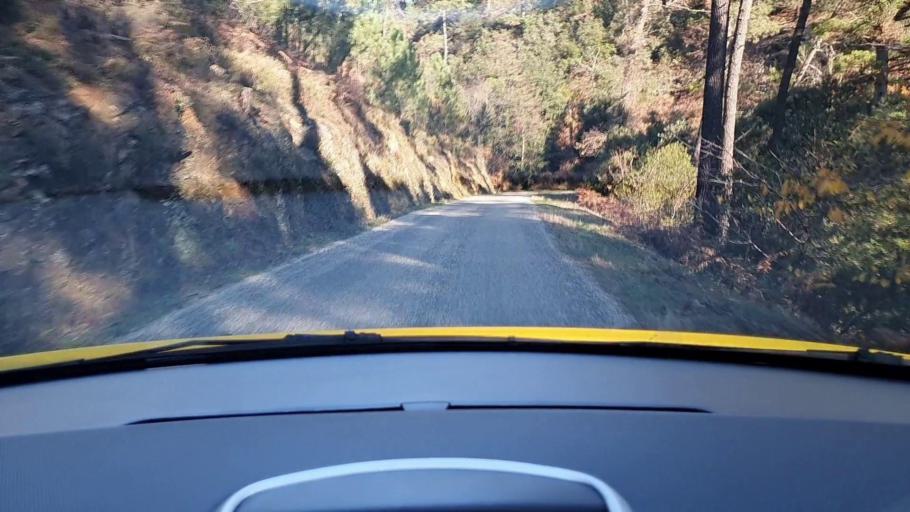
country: FR
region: Languedoc-Roussillon
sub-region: Departement du Gard
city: Branoux-les-Taillades
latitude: 44.2366
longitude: 3.9780
